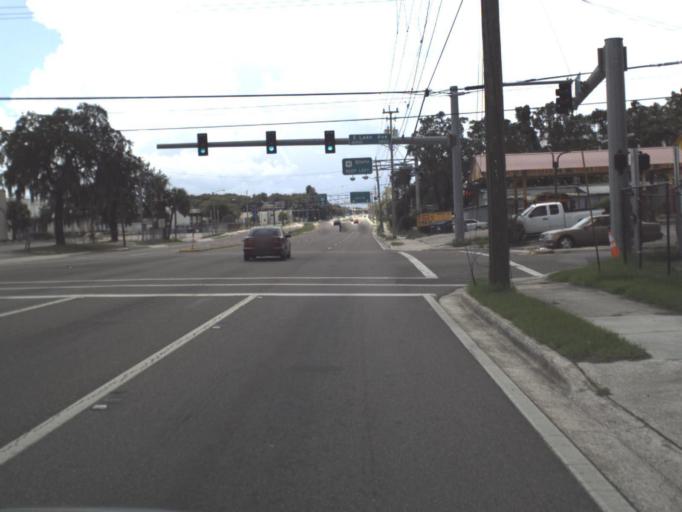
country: US
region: Florida
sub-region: Hillsborough County
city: East Lake-Orient Park
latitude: 27.9781
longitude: -82.4142
